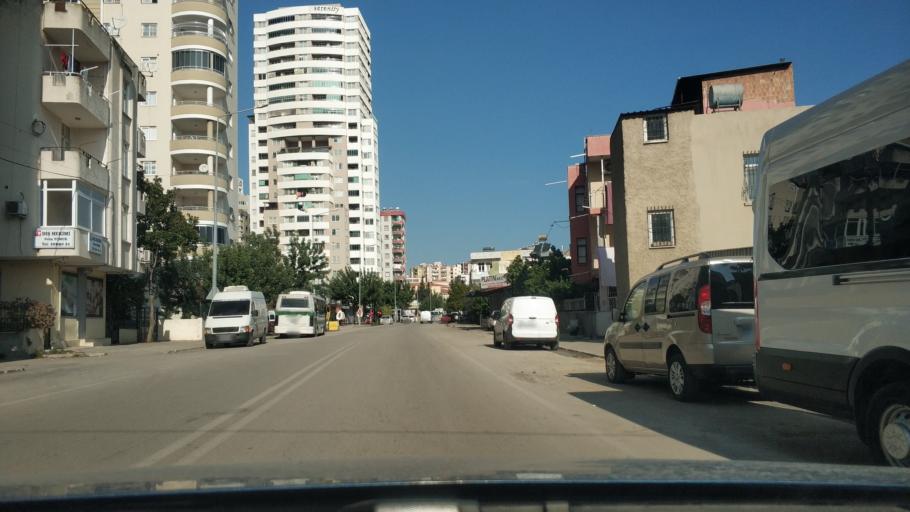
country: TR
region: Adana
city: Seyhan
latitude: 37.0195
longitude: 35.2913
